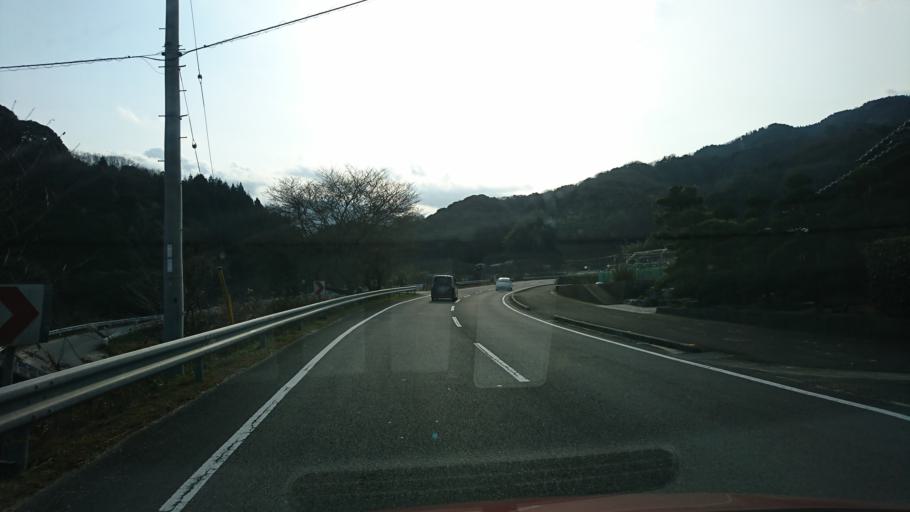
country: JP
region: Ehime
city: Hojo
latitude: 33.9884
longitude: 132.9107
